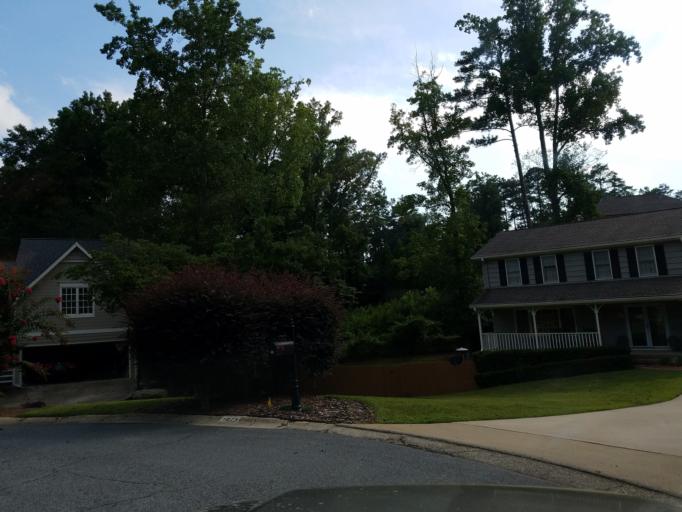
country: US
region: Georgia
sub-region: Fulton County
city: Sandy Springs
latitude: 33.9759
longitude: -84.4418
